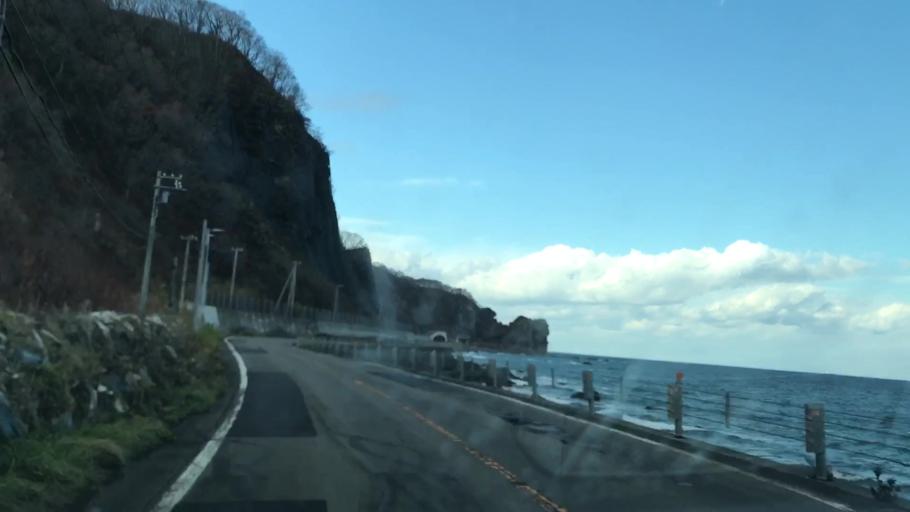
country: JP
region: Hokkaido
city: Iwanai
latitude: 43.3290
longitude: 140.4225
